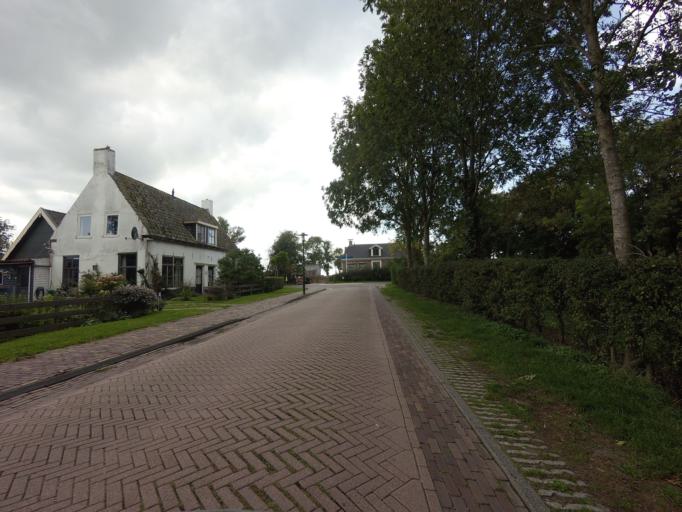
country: NL
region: Friesland
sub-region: Sudwest Fryslan
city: Bolsward
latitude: 53.0682
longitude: 5.5689
